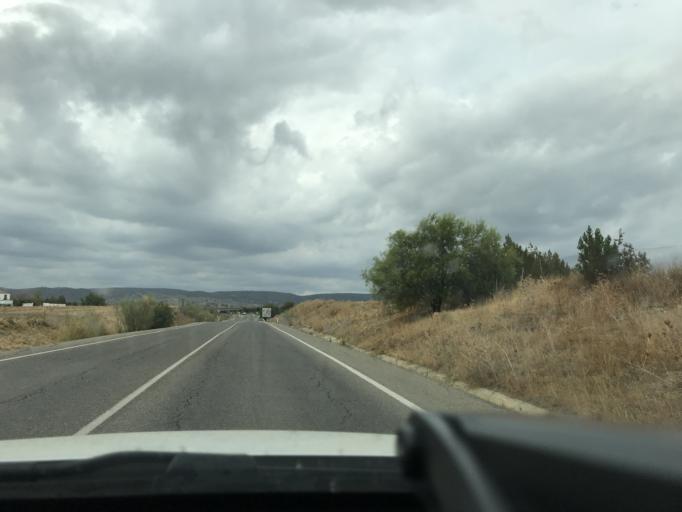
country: ES
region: Andalusia
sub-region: Provincia de Sevilla
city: Cantillana
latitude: 37.6169
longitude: -5.8112
